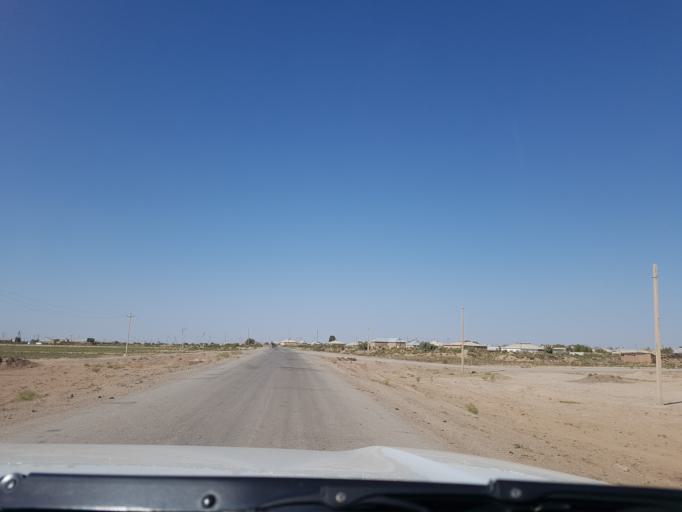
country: IR
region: Razavi Khorasan
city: Sarakhs
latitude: 36.5114
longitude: 61.2532
